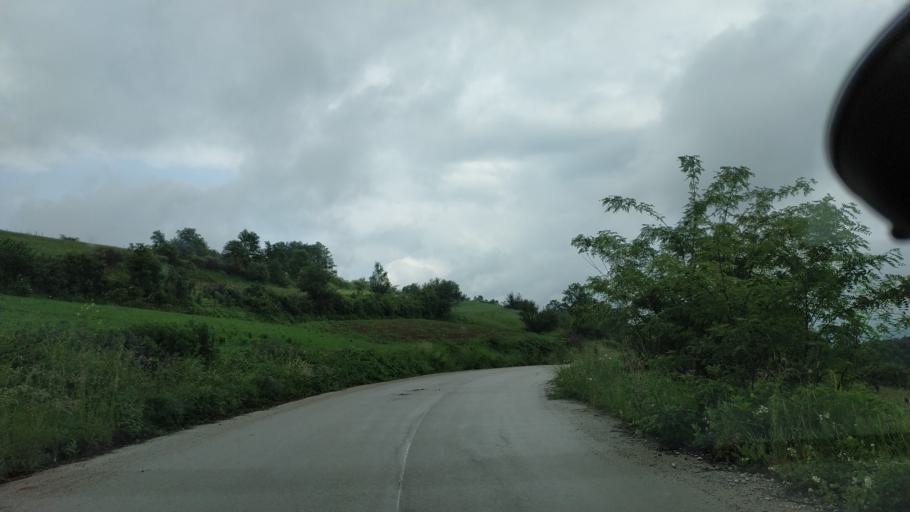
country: RS
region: Central Serbia
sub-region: Toplicki Okrug
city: Prokuplje
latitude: 43.4113
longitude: 21.5517
